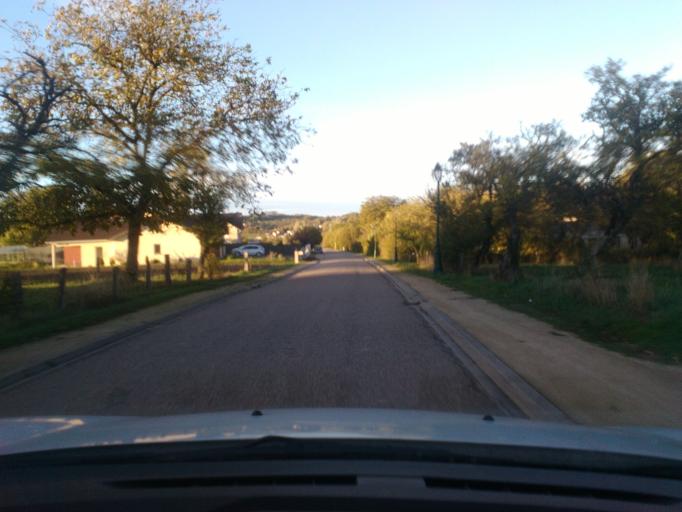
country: FR
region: Lorraine
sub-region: Departement des Vosges
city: Charmes
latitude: 48.3498
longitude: 6.2549
